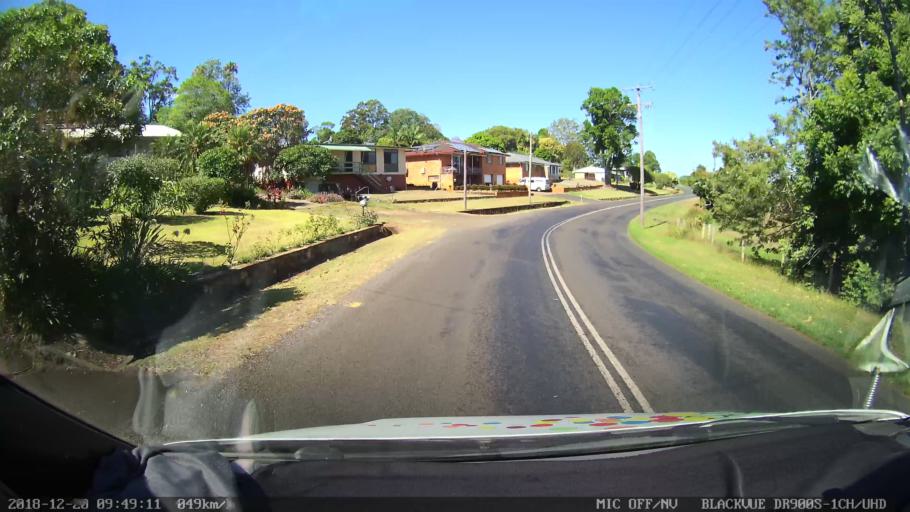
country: AU
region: New South Wales
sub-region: Lismore Municipality
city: Lismore
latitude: -28.7737
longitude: 153.2875
